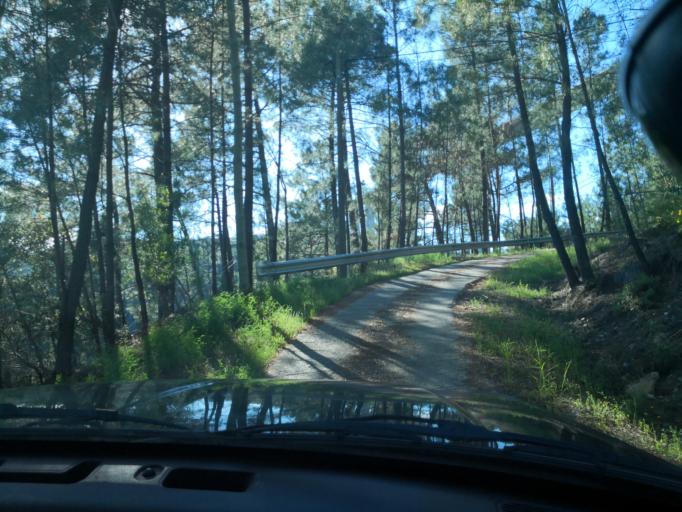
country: PT
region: Vila Real
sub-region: Vila Real
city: Vila Real
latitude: 41.2758
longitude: -7.7481
